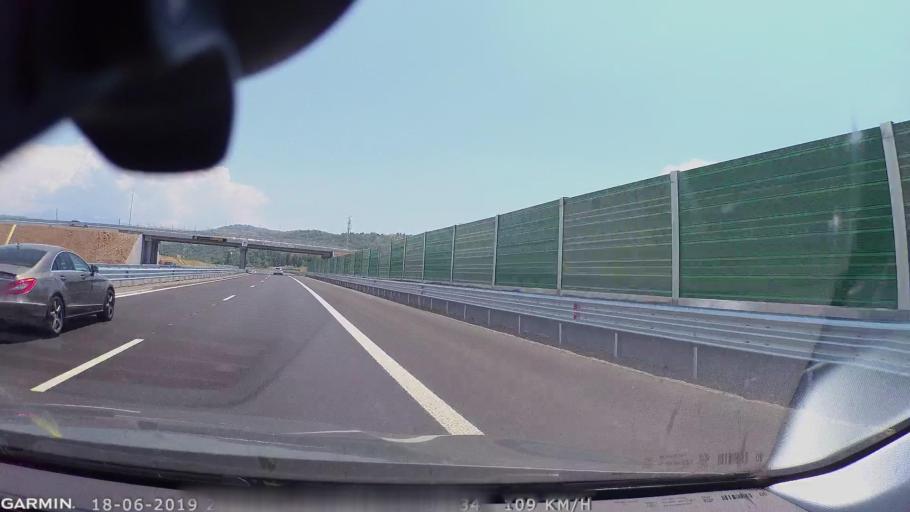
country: BG
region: Blagoevgrad
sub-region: Obshtina Blagoevgrad
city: Blagoevgrad
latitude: 41.9869
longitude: 23.0566
